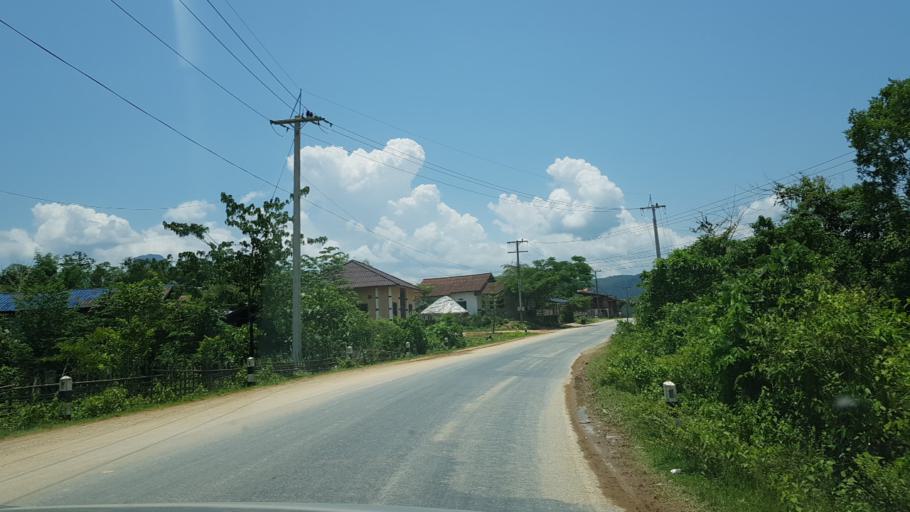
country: LA
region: Vientiane
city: Muang Kasi
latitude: 19.2516
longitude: 102.2472
